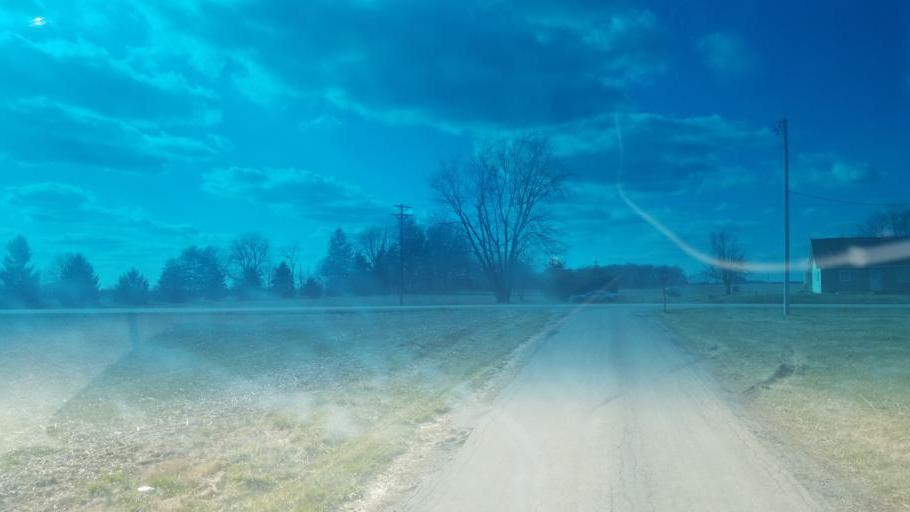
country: US
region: Ohio
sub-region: Highland County
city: Greenfield
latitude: 39.3175
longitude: -83.4241
